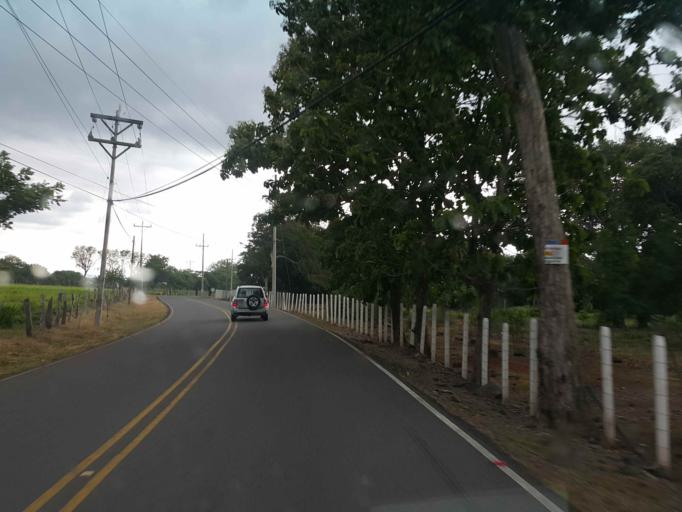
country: CR
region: Puntarenas
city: Miramar
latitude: 10.0998
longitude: -84.8217
